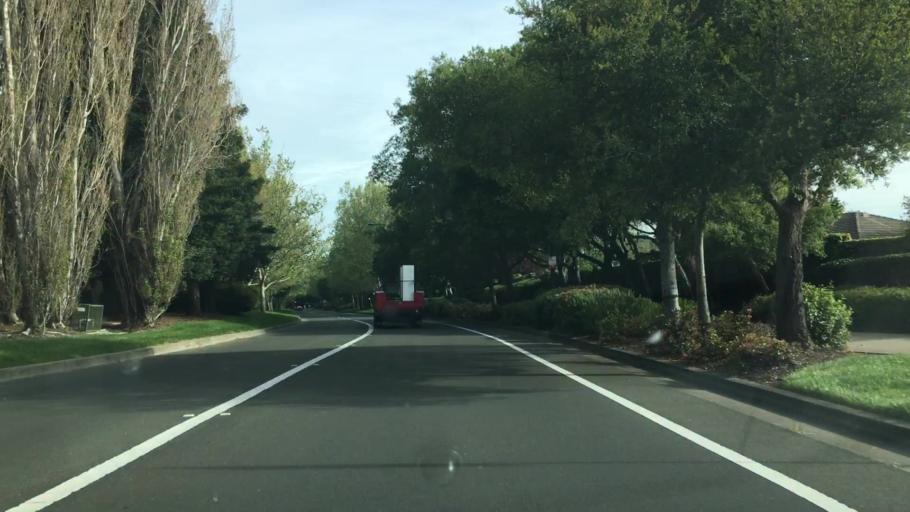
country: US
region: California
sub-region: Solano County
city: Green Valley
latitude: 38.2263
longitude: -122.1472
